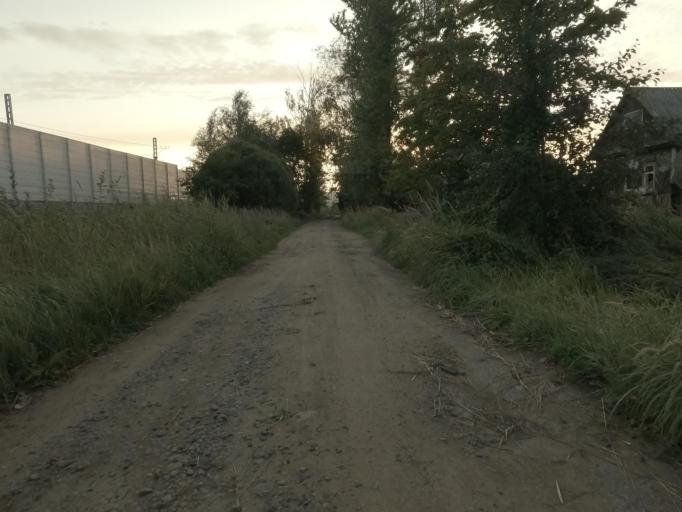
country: RU
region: Leningrad
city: Mga
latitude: 59.7580
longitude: 31.0442
